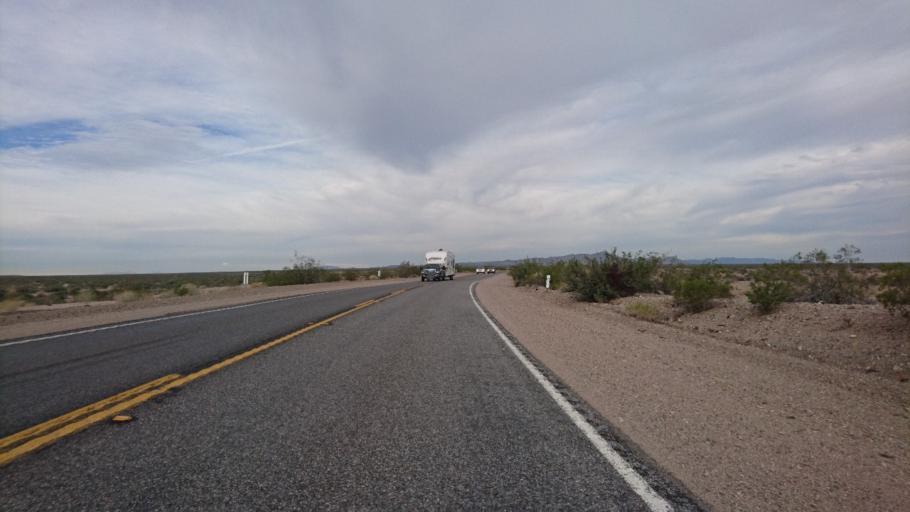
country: US
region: Arizona
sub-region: Mohave County
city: Willow Valley
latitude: 34.9360
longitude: -114.8059
